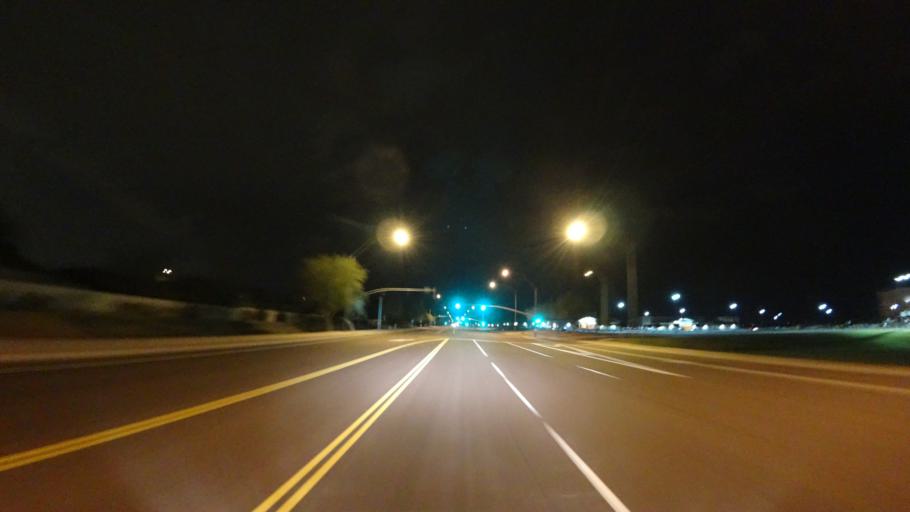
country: US
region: Arizona
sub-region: Pinal County
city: Apache Junction
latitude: 33.3668
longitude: -111.6187
